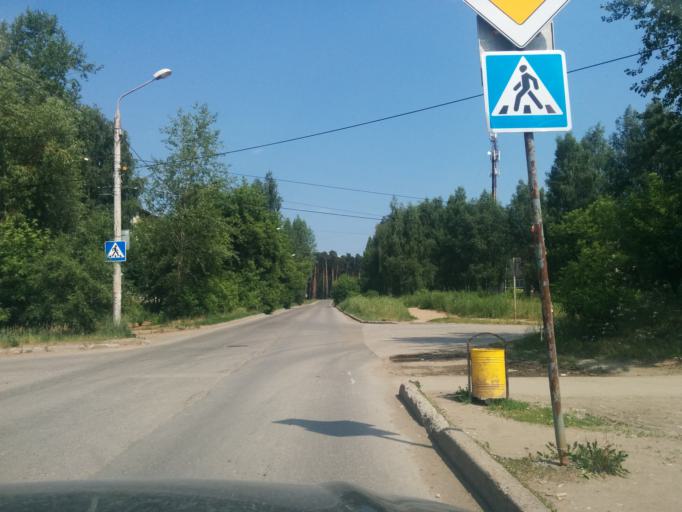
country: RU
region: Perm
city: Kondratovo
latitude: 58.0267
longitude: 56.0107
